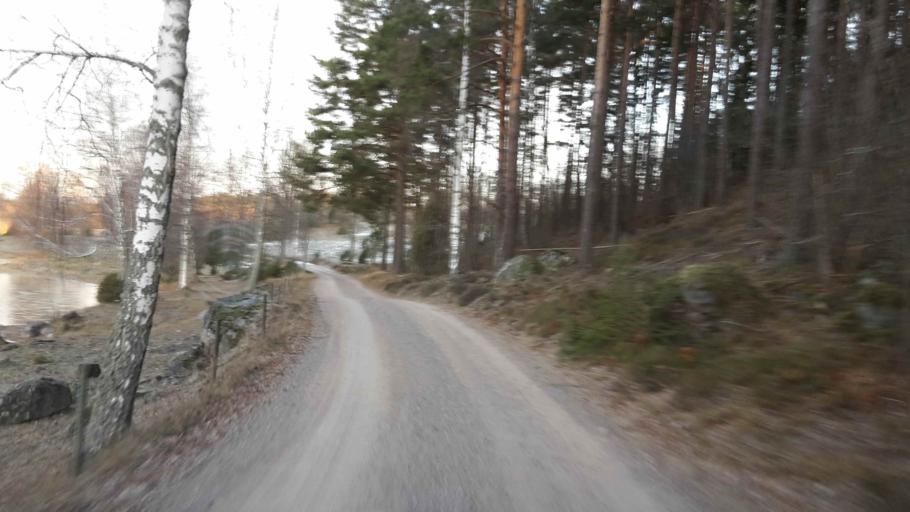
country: SE
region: OEstergoetland
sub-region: Atvidabergs Kommun
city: Atvidaberg
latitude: 58.2712
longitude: 16.1210
